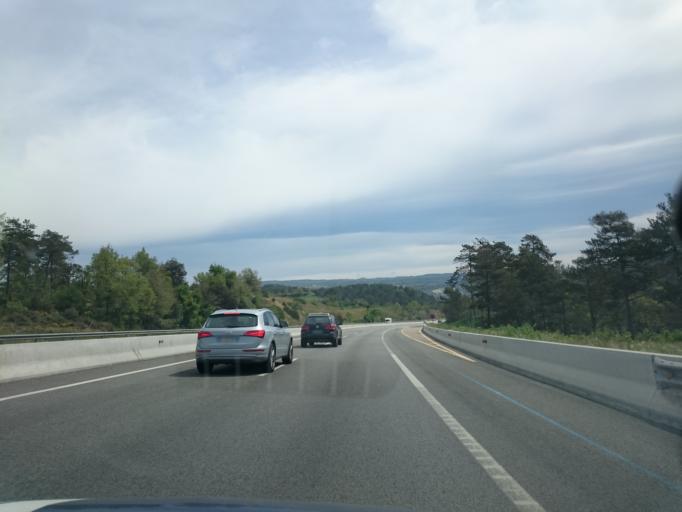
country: ES
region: Catalonia
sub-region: Provincia de Barcelona
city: Muntanyola
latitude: 41.9305
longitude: 2.1489
